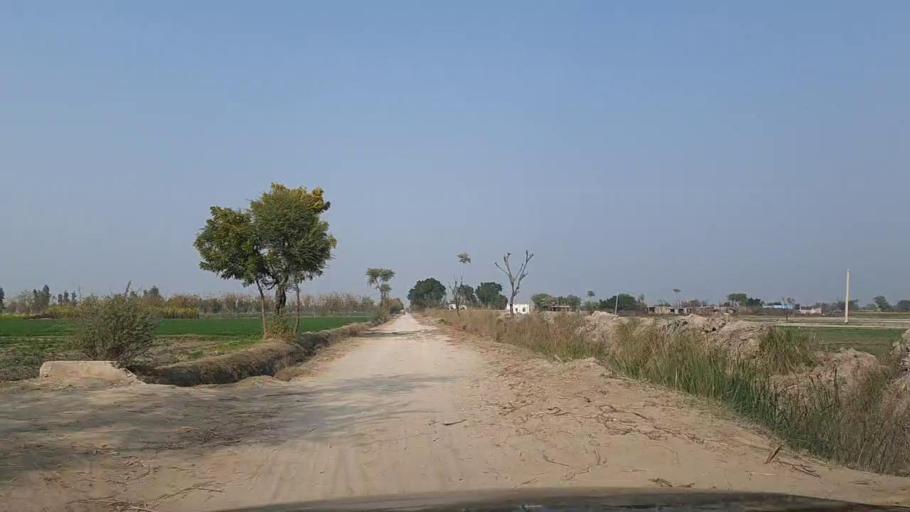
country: PK
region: Sindh
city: Daur
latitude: 26.3959
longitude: 68.4238
